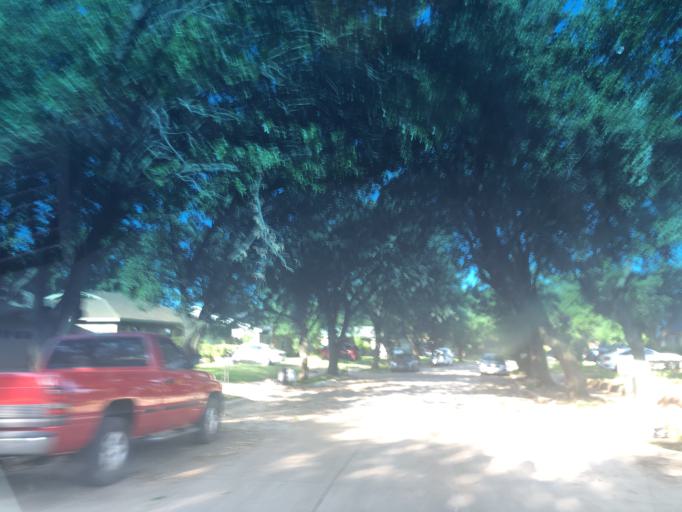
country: US
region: Texas
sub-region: Dallas County
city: Grand Prairie
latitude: 32.7022
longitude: -97.0005
